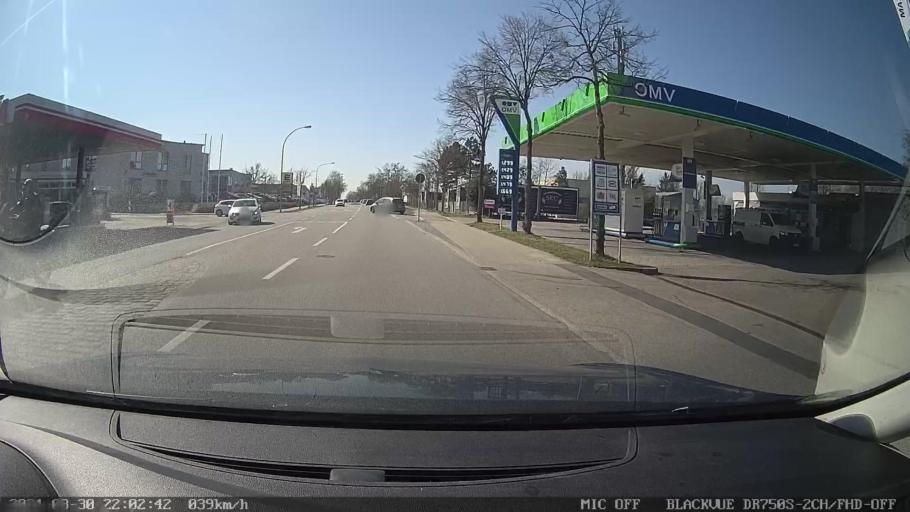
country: DE
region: Bavaria
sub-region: Upper Palatinate
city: Regenstauf
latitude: 49.1193
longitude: 12.1263
